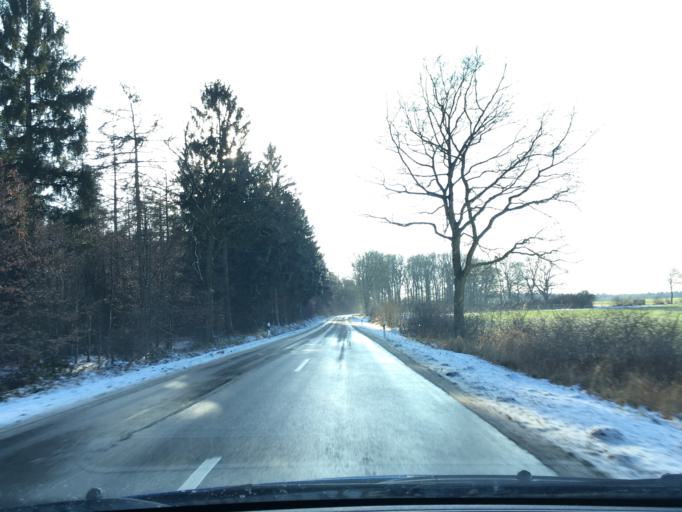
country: DE
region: Schleswig-Holstein
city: Wiershop
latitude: 53.4247
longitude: 10.4522
